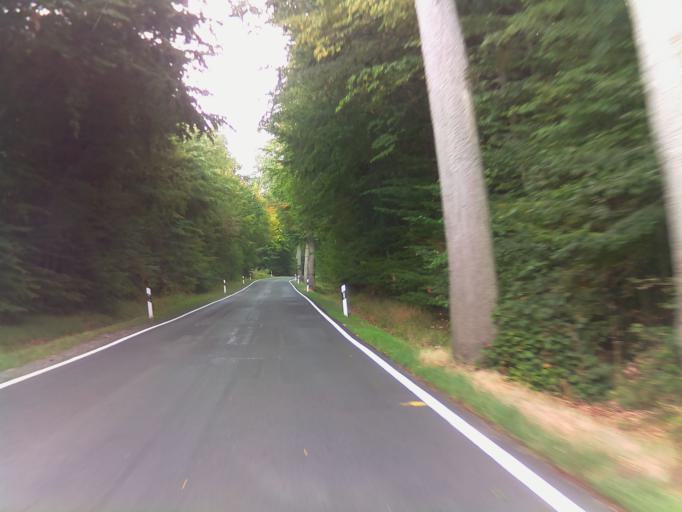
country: DE
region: Hesse
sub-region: Regierungsbezirk Giessen
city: Lauterbach
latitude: 50.5728
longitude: 9.4314
